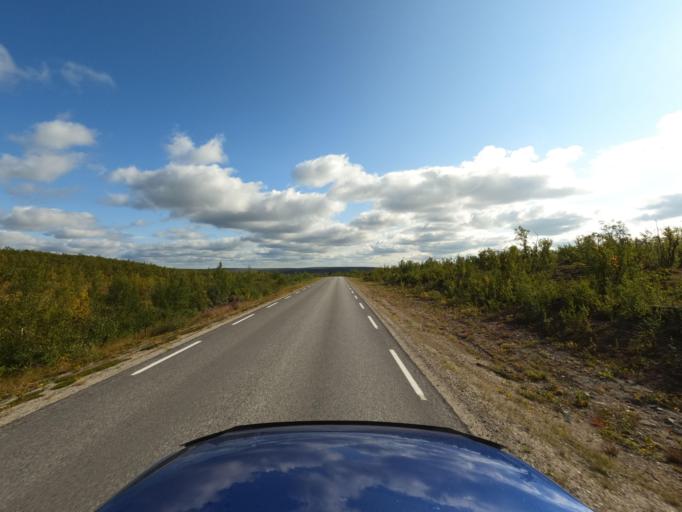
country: NO
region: Finnmark Fylke
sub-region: Porsanger
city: Lakselv
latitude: 69.3938
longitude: 24.5739
